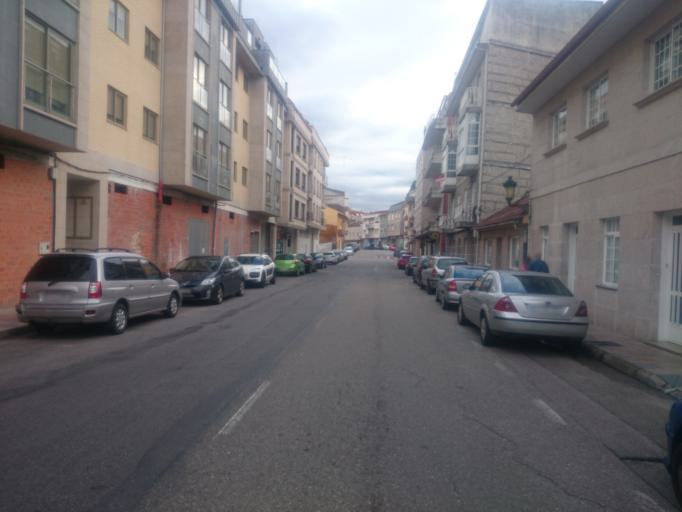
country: ES
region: Galicia
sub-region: Provincia de Pontevedra
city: Porrino
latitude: 42.1567
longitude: -8.6205
